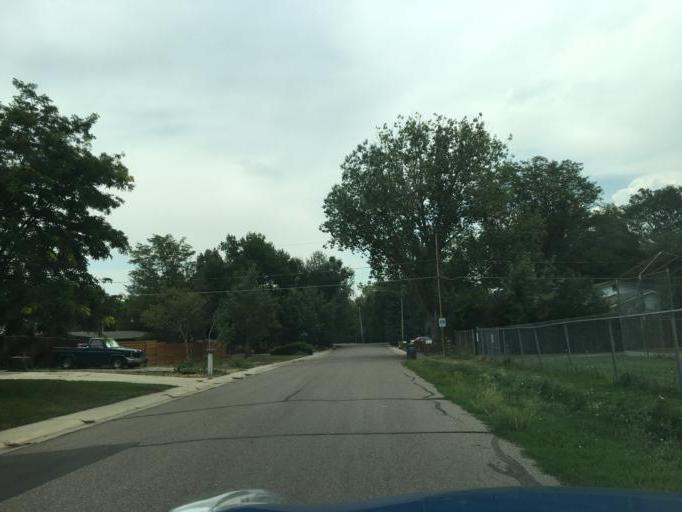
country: US
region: Colorado
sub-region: Jefferson County
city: Wheat Ridge
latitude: 39.7530
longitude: -105.0926
